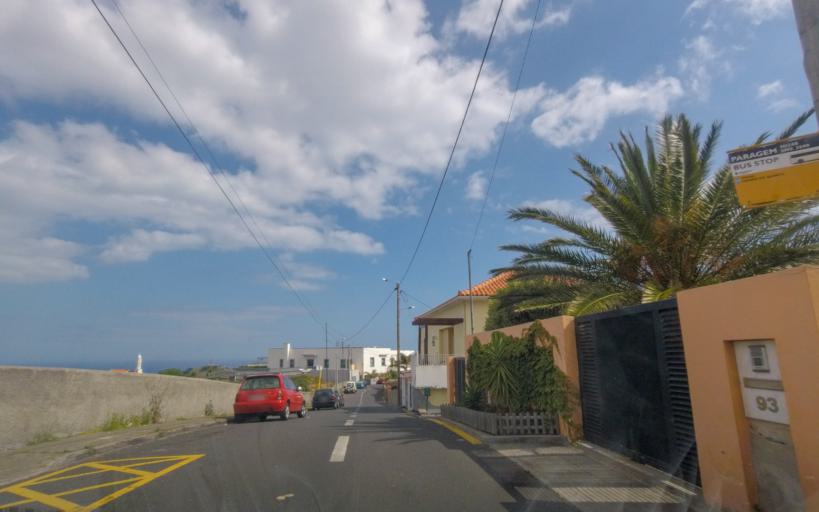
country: PT
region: Madeira
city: Camara de Lobos
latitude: 32.6539
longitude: -16.9501
